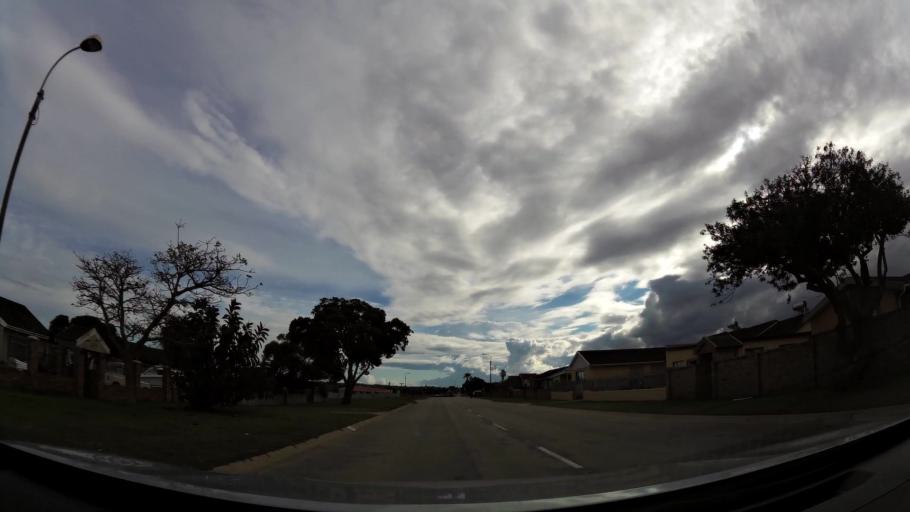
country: ZA
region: Eastern Cape
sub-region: Nelson Mandela Bay Metropolitan Municipality
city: Port Elizabeth
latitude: -33.9421
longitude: 25.4807
